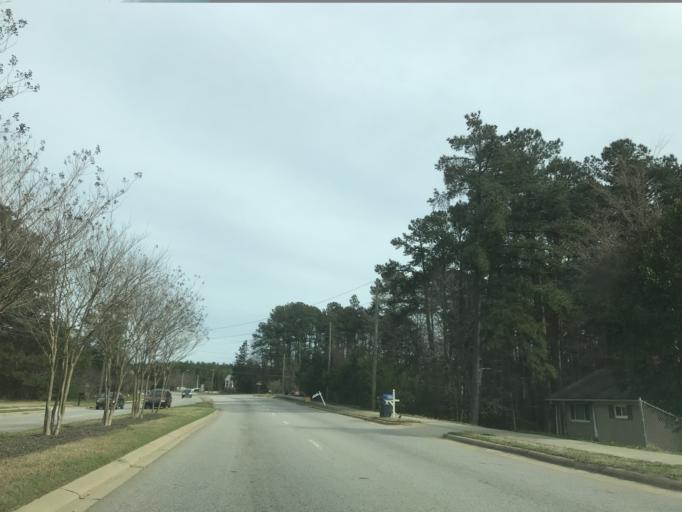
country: US
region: North Carolina
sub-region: Wake County
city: West Raleigh
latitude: 35.7435
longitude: -78.6878
